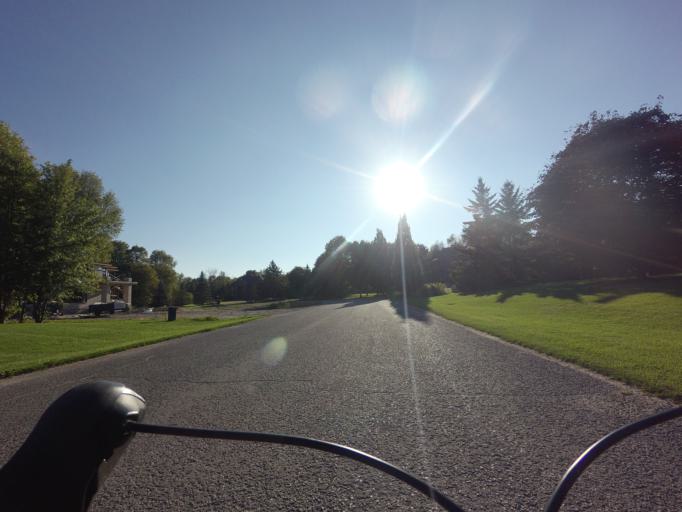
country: CA
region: Ontario
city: Bells Corners
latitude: 45.2190
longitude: -75.7003
